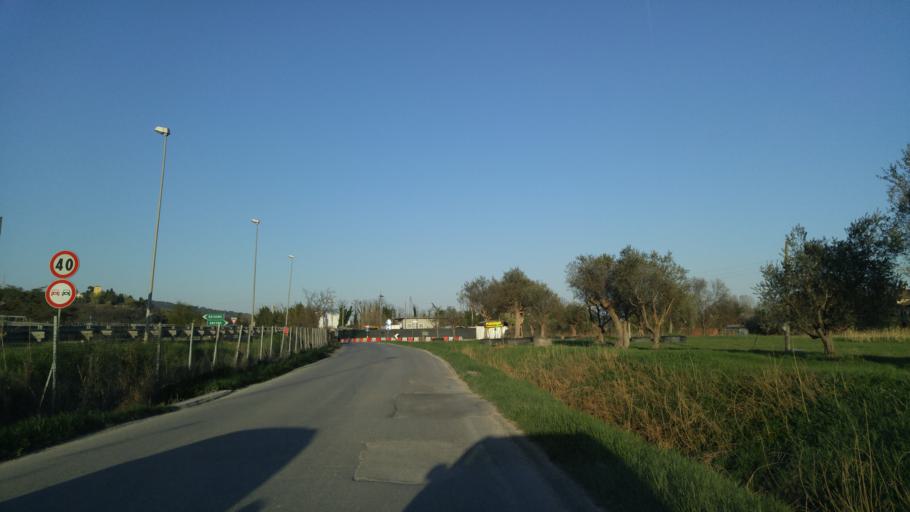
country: IT
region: The Marches
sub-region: Provincia di Pesaro e Urbino
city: Villa Ceccolini
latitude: 43.8976
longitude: 12.8428
